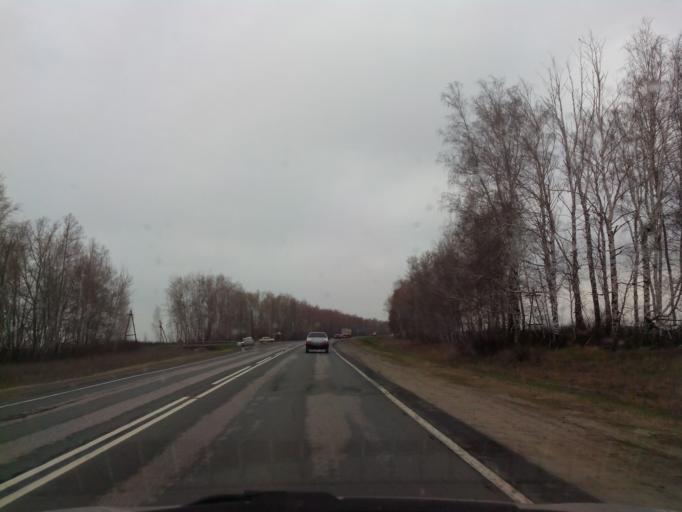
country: RU
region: Tambov
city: Pervomayskiy
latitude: 53.0922
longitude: 40.3980
